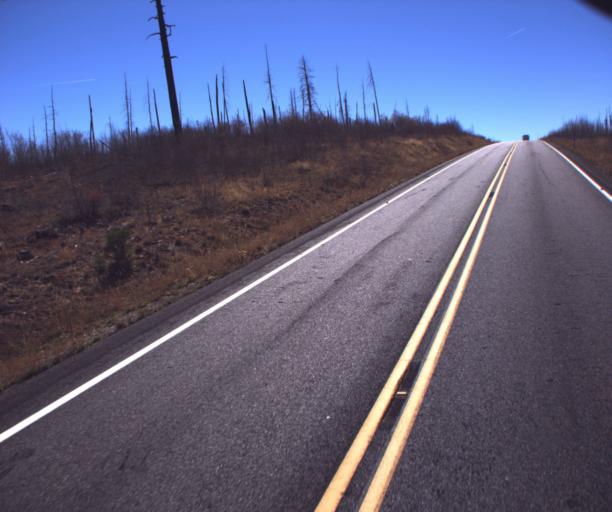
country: US
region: Arizona
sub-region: Coconino County
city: Fredonia
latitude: 36.5948
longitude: -112.1788
